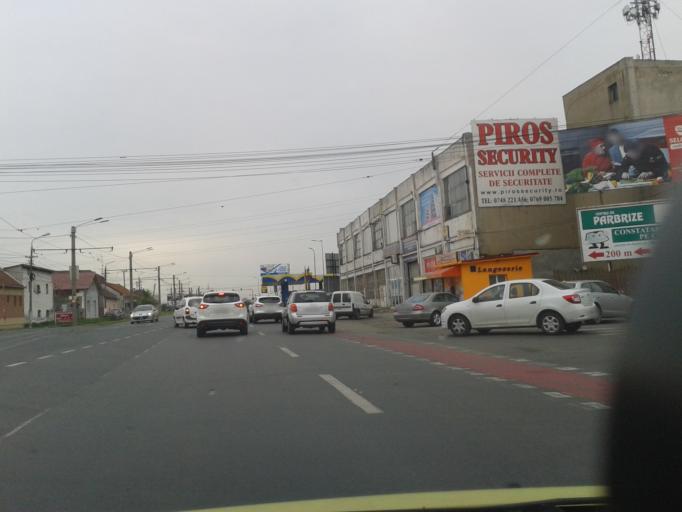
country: RO
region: Arad
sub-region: Comuna Vladimirescu
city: Vladimirescu
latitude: 46.1754
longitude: 21.3652
